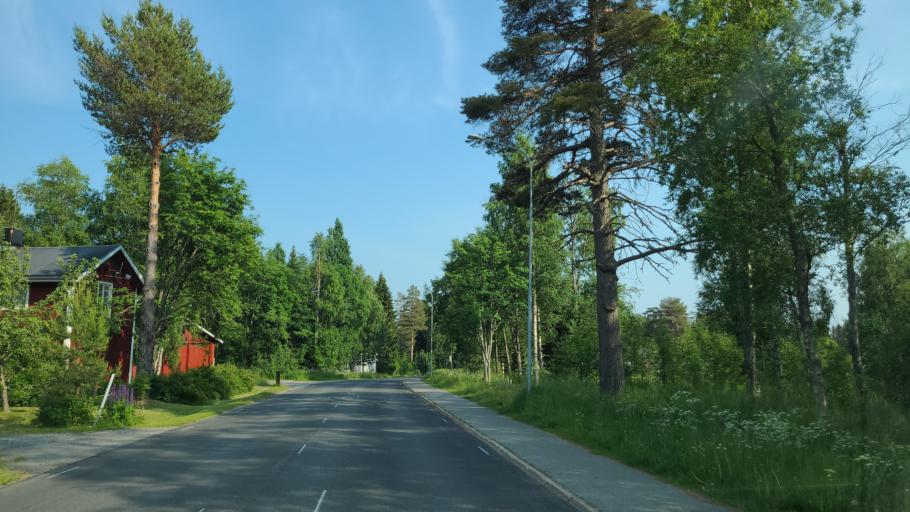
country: SE
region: Vaesterbotten
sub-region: Skelleftea Kommun
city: Burea
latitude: 64.3654
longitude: 21.3277
